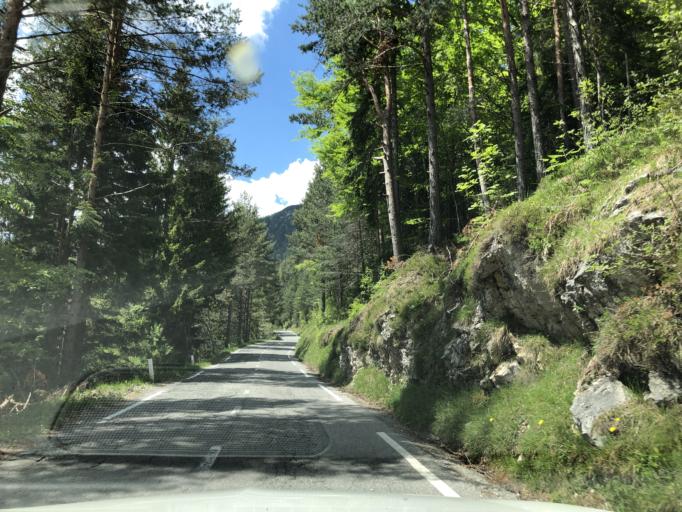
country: IT
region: Friuli Venezia Giulia
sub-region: Provincia di Udine
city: Tarvisio
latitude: 46.4188
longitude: 13.6064
